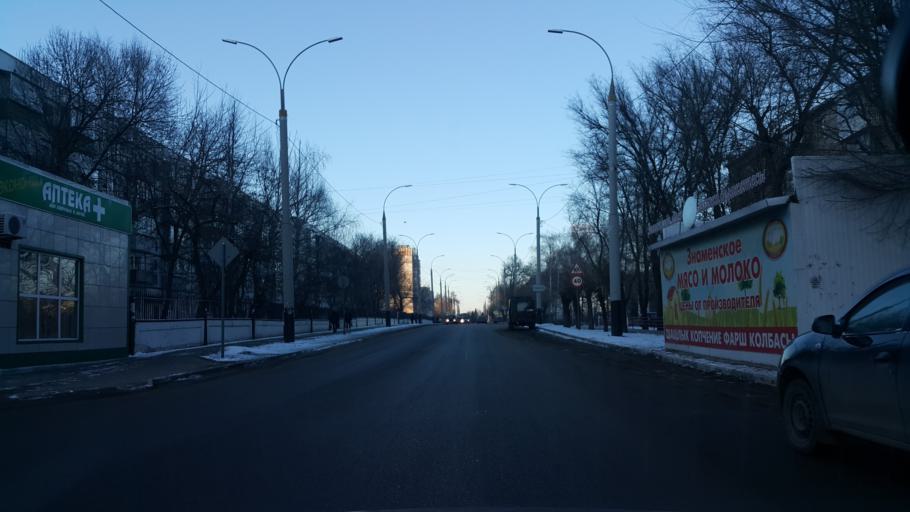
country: RU
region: Tambov
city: Pokrovo-Prigorodnoye
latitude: 52.7053
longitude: 41.3990
